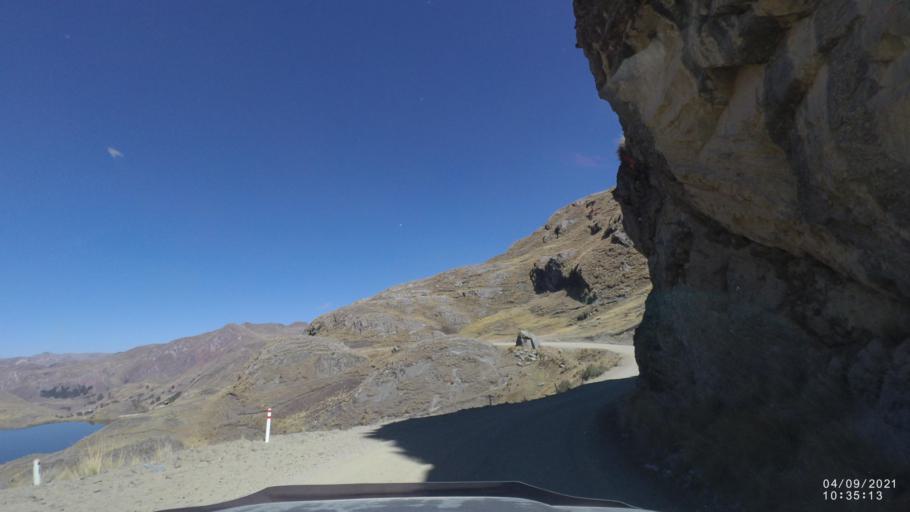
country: BO
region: Cochabamba
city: Sipe Sipe
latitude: -17.2900
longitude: -66.4463
